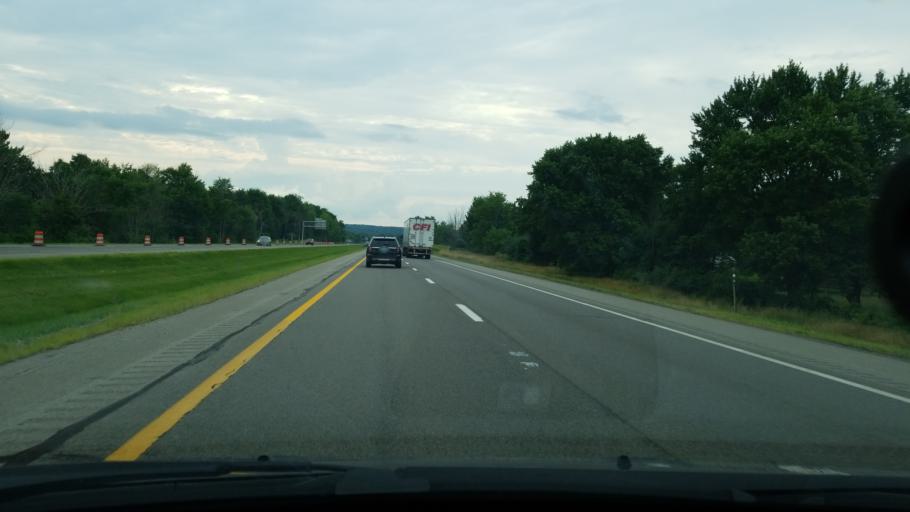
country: US
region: Ohio
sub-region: Mahoning County
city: Boardman
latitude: 40.9718
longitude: -80.6627
